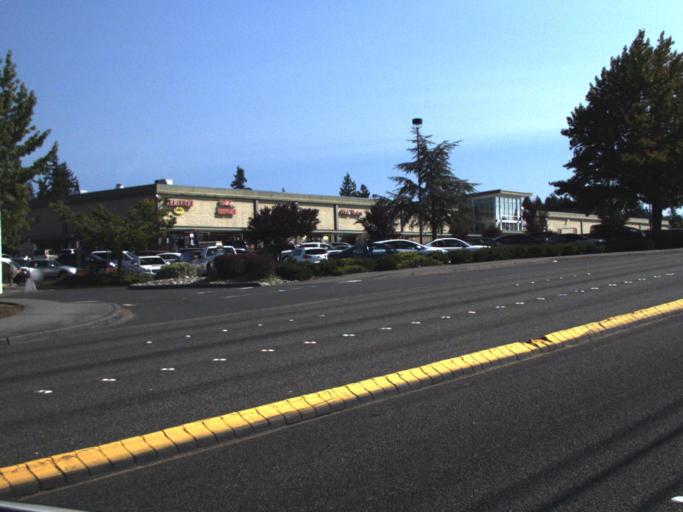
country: US
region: Washington
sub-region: Snohomish County
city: Alderwood Manor
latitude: 47.8210
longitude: -122.2972
